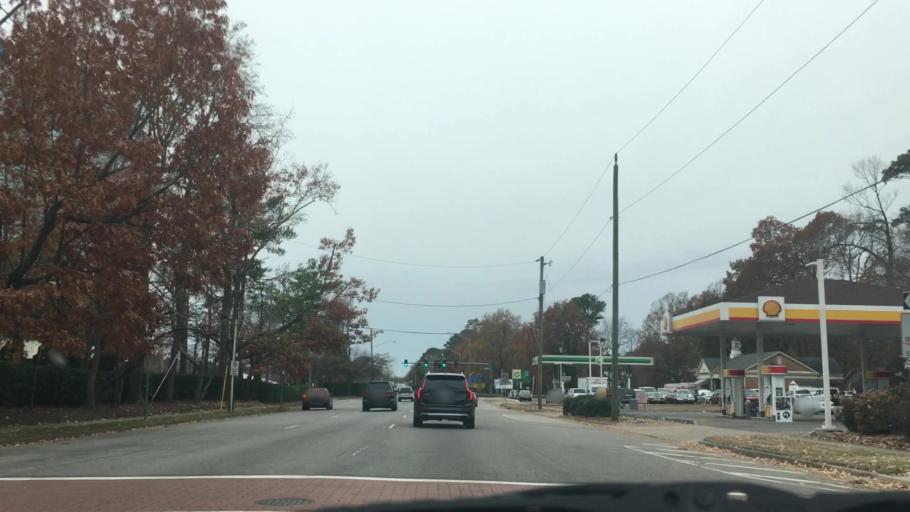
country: US
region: Virginia
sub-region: City of Virginia Beach
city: Virginia Beach
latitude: 36.8487
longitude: -75.9844
